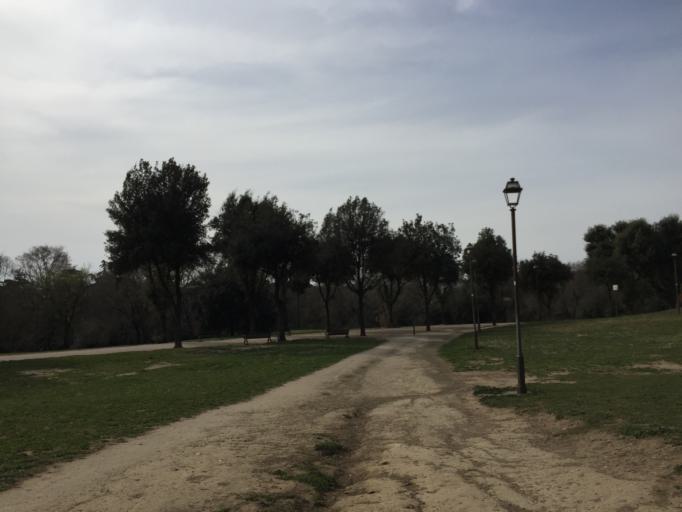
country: VA
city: Vatican City
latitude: 41.8870
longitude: 12.4552
